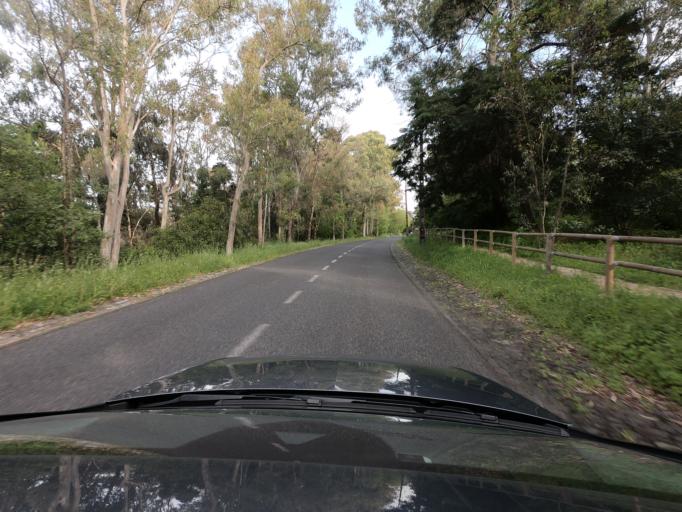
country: PT
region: Setubal
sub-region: Almada
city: Pragal
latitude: 38.7190
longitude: -9.1818
